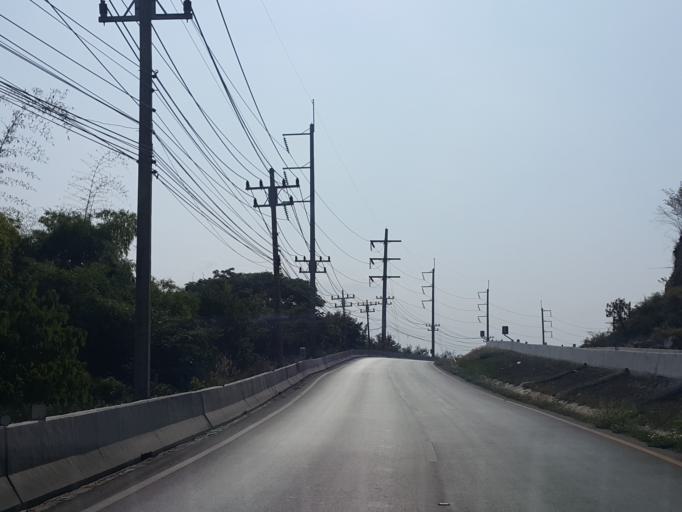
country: TH
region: Chiang Mai
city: Chom Thong
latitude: 18.3829
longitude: 98.6794
